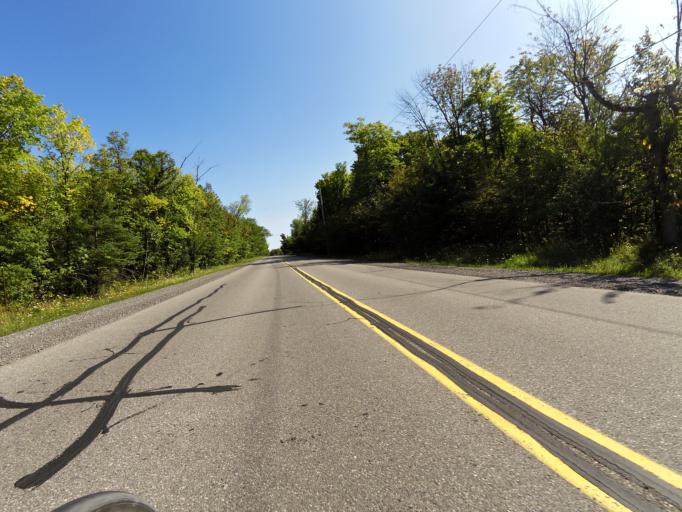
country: CA
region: Ontario
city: Bells Corners
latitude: 45.4241
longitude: -75.9515
